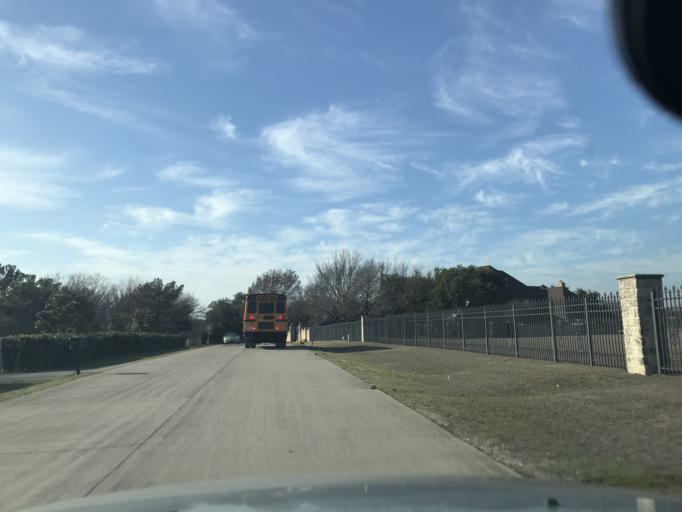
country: US
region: Texas
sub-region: Denton County
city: The Colony
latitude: 33.0975
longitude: -96.8334
